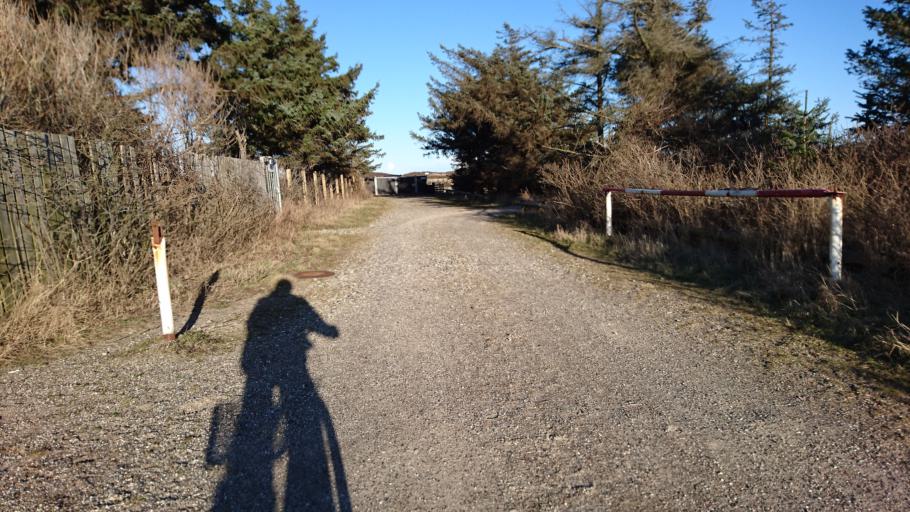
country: DK
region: North Denmark
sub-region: Frederikshavn Kommune
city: Skagen
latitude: 57.7300
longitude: 10.6141
